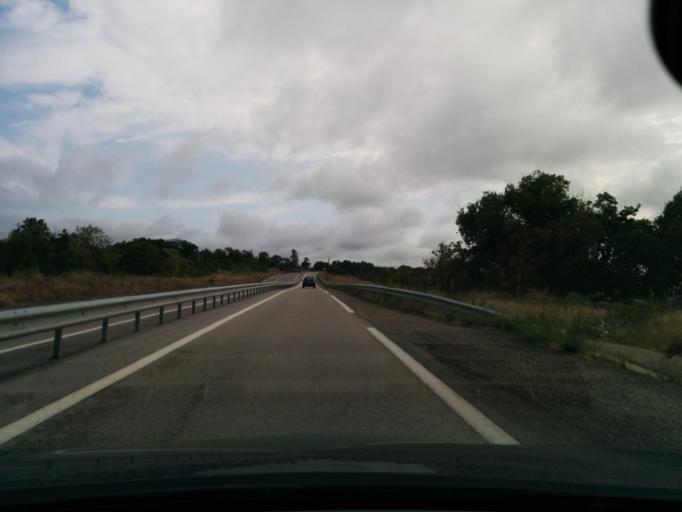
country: FR
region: Midi-Pyrenees
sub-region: Departement du Lot
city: Pradines
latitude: 44.4997
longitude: 1.4413
